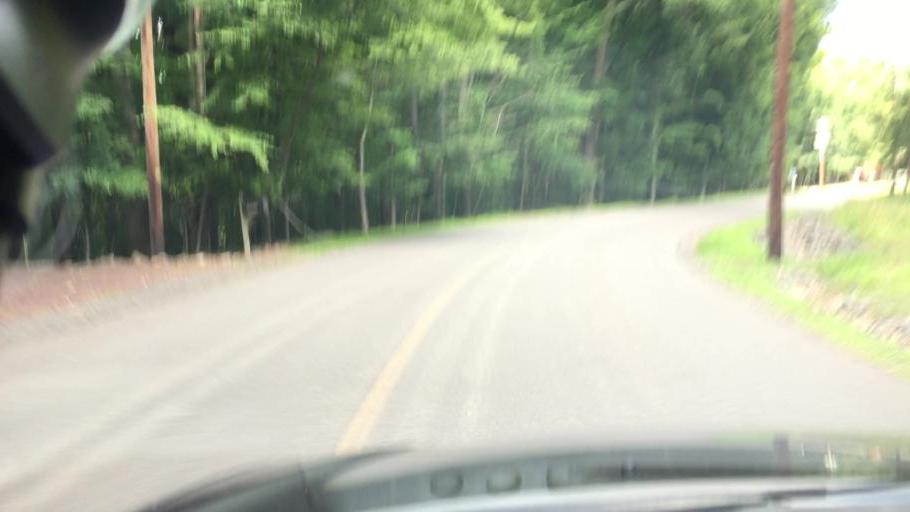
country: US
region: Pennsylvania
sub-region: Luzerne County
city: Freeland
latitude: 41.0472
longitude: -75.9183
